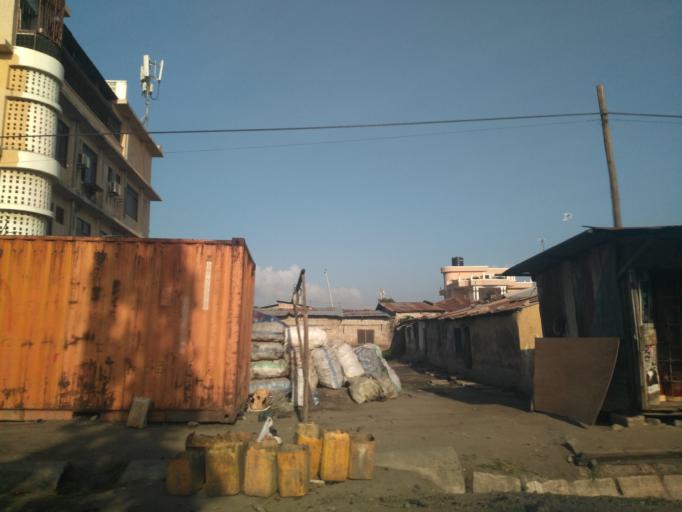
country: TZ
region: Dar es Salaam
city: Magomeni
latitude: -6.7867
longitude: 39.2654
